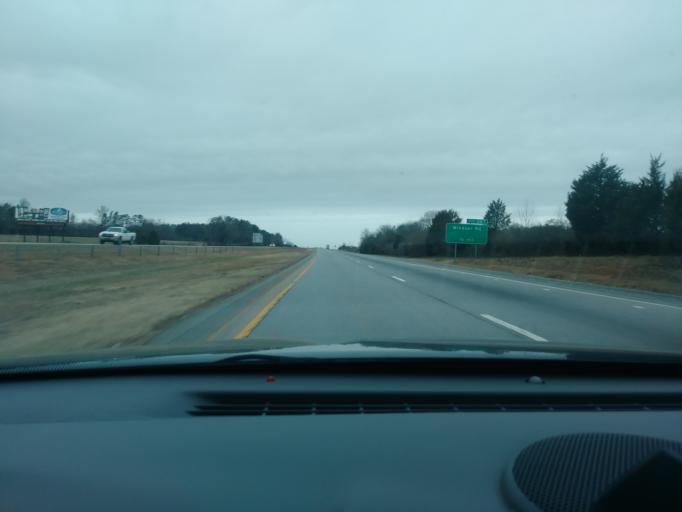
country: US
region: North Carolina
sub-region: Yadkin County
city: Jonesville
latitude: 36.1242
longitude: -80.8213
